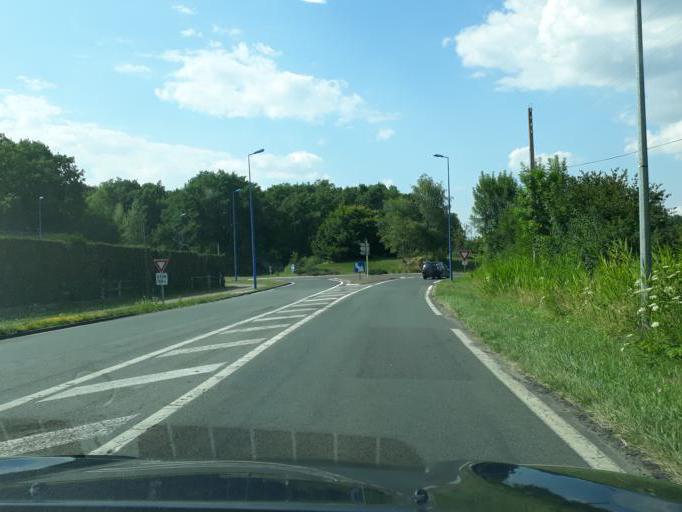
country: FR
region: Bourgogne
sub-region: Departement de la Nievre
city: Fourchambault
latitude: 47.0047
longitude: 3.0961
